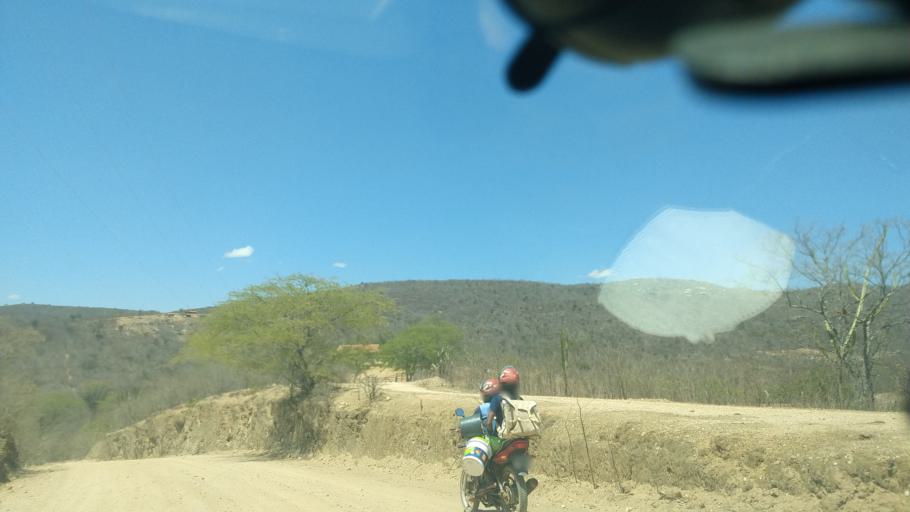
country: BR
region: Rio Grande do Norte
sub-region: Cerro Cora
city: Cerro Cora
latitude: -6.0156
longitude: -36.3088
